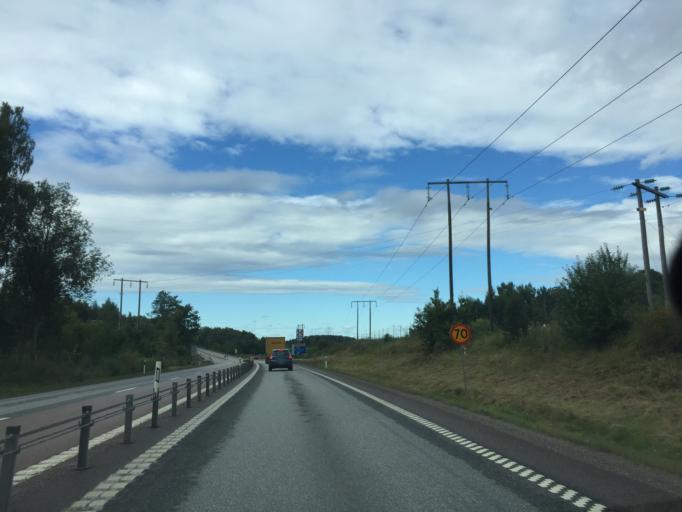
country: SE
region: Vaestmanland
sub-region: Kungsors Kommun
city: Kungsoer
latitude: 59.4165
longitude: 16.0714
